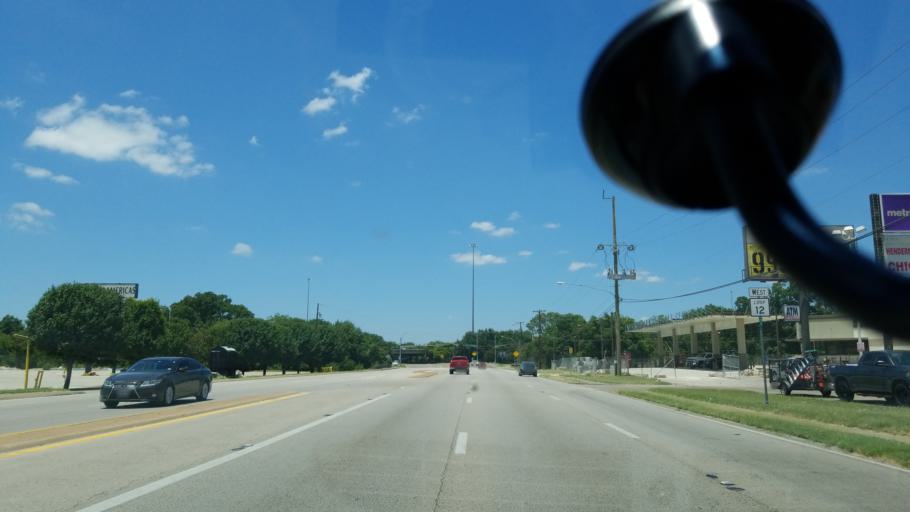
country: US
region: Texas
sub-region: Dallas County
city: Cockrell Hill
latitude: 32.6854
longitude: -96.8193
